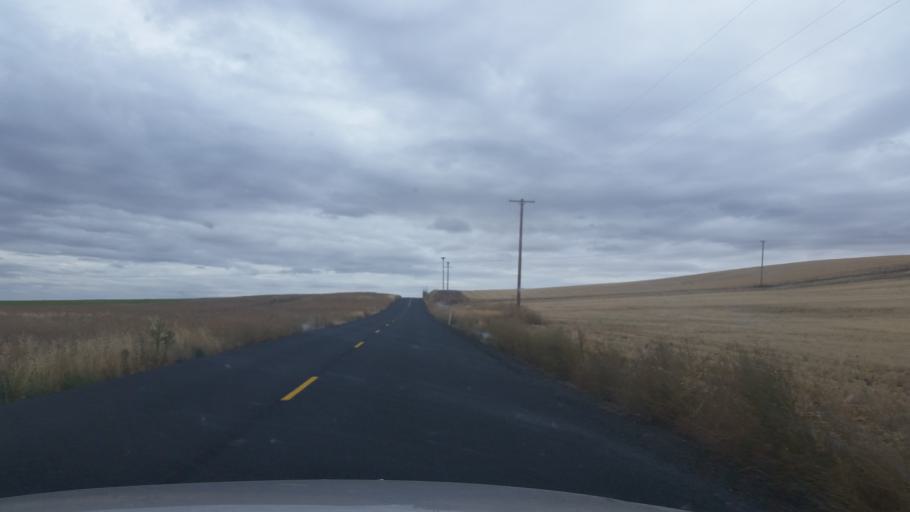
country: US
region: Washington
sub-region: Spokane County
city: Medical Lake
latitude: 47.5145
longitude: -117.7231
